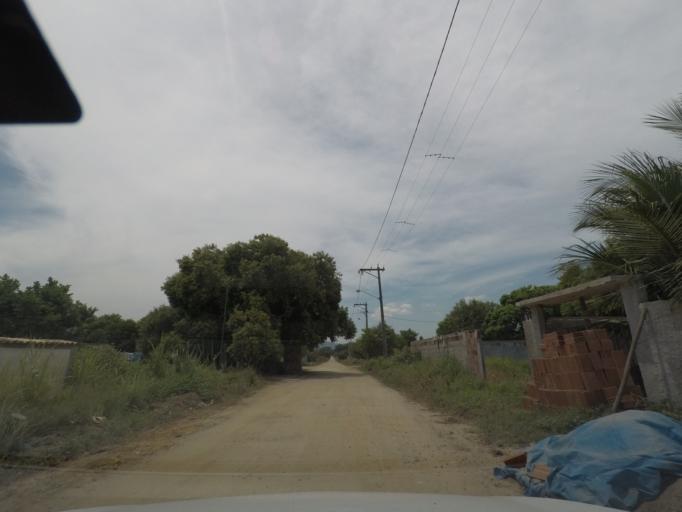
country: BR
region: Rio de Janeiro
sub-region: Marica
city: Marica
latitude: -22.9549
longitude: -42.9456
